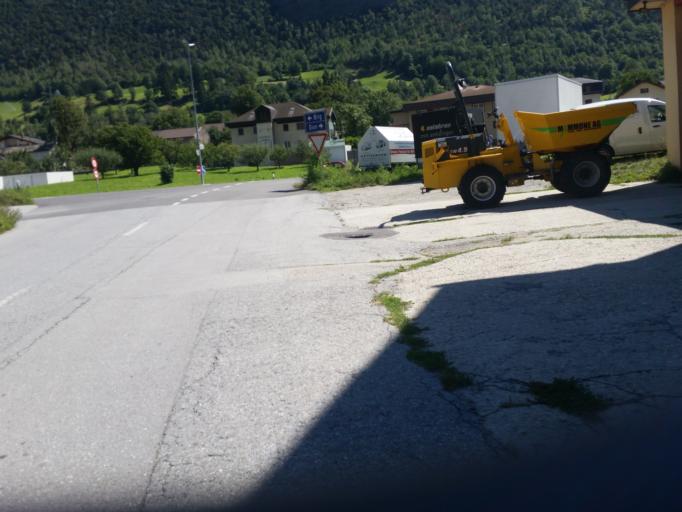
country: CH
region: Valais
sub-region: Brig District
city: Brig
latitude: 46.3065
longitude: 7.9534
